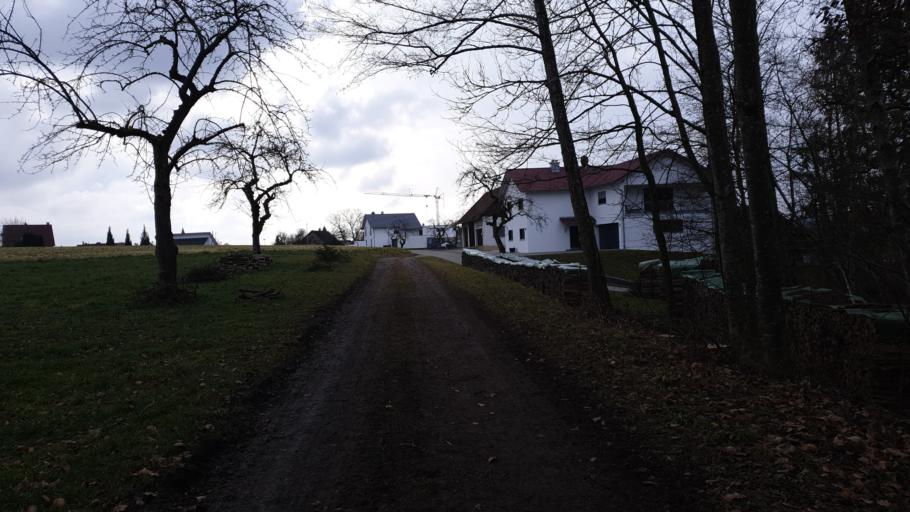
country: DE
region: Baden-Wuerttemberg
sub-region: Tuebingen Region
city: Wolpertswende
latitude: 47.8816
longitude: 9.6309
